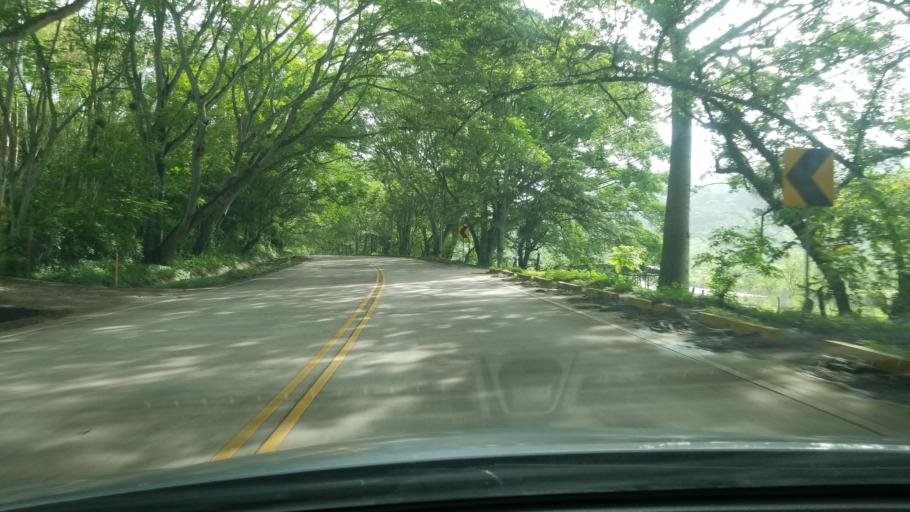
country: HN
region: Copan
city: Copan
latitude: 14.8474
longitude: -89.1333
